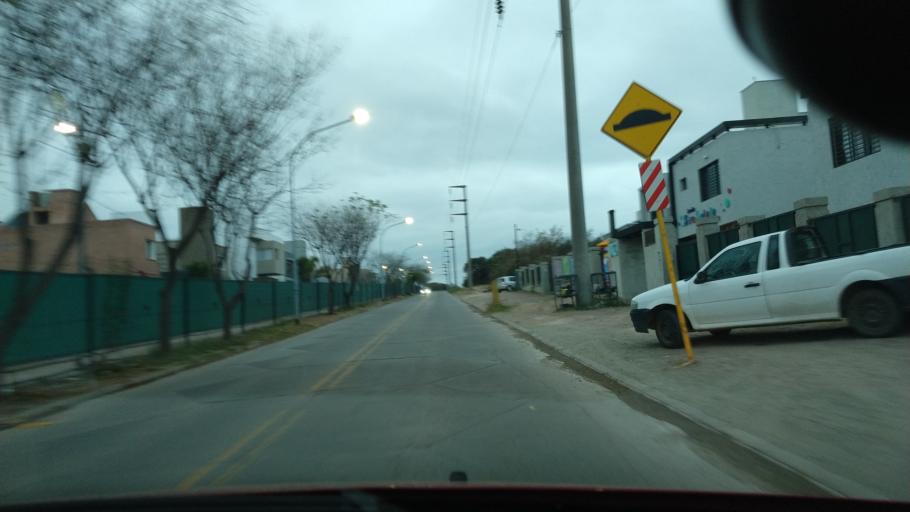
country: AR
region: Cordoba
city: La Calera
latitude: -31.3785
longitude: -64.2725
